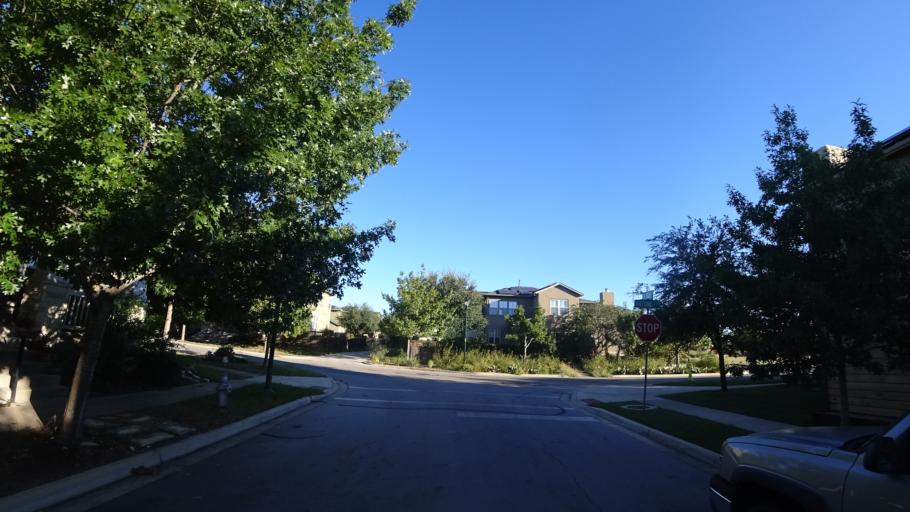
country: US
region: Texas
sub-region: Travis County
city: Austin
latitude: 30.2912
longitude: -97.7034
